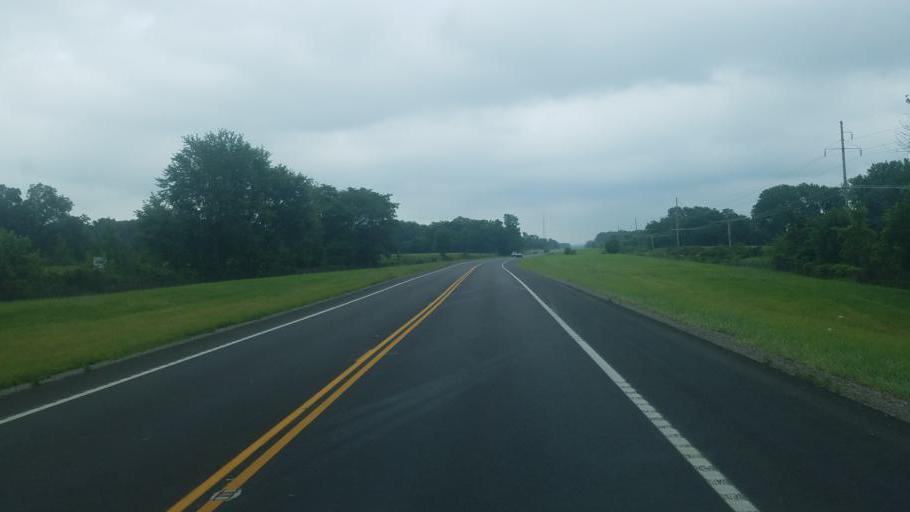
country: US
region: Ohio
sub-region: Logan County
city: Russells Point
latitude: 40.4637
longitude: -83.8737
